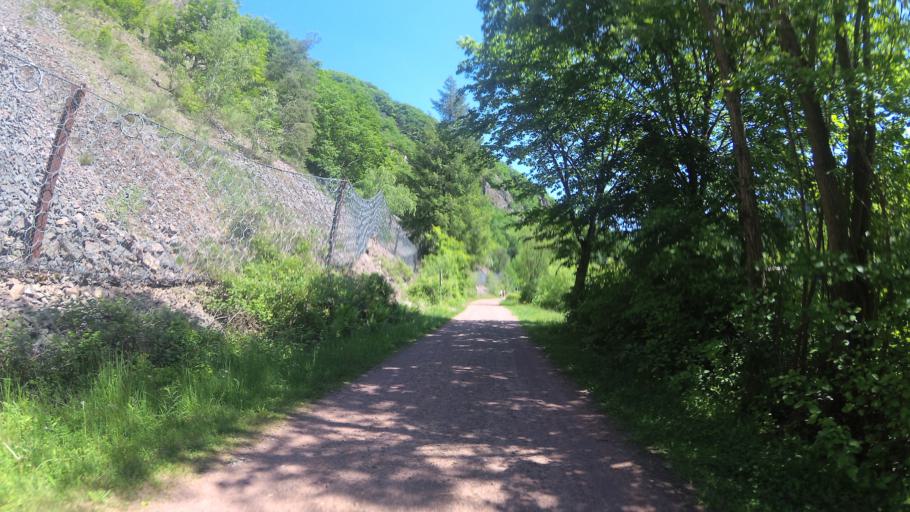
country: DE
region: Saarland
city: Orscholz
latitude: 49.5029
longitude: 6.5507
